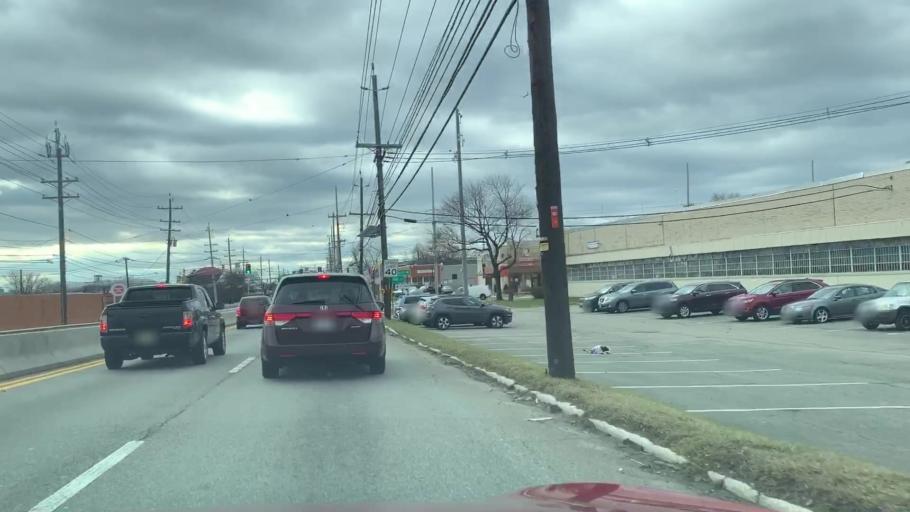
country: US
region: New Jersey
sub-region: Bergen County
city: Moonachie
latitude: 40.8236
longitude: -74.0597
